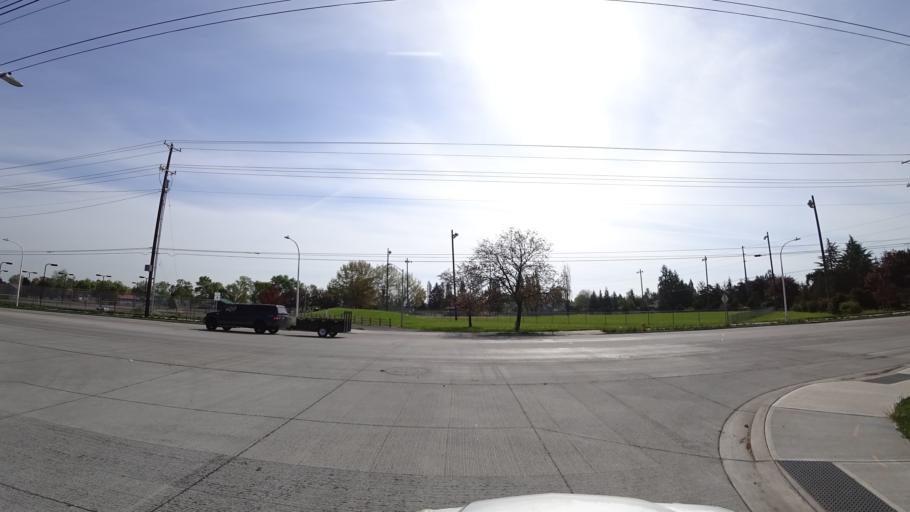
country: US
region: Oregon
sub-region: Washington County
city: Hillsboro
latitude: 45.5266
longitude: -122.9543
